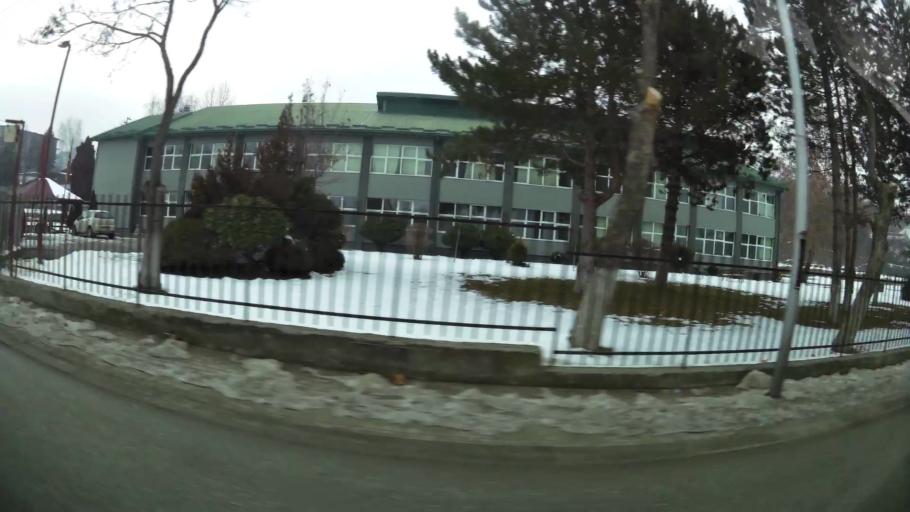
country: MK
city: Kondovo
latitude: 42.0117
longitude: 21.3074
